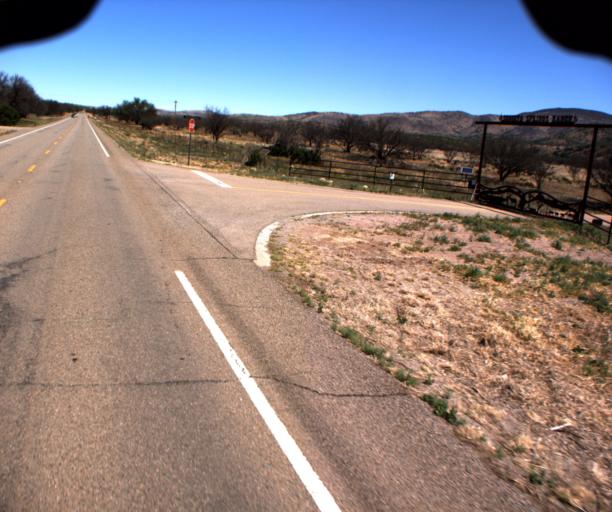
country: US
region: Arizona
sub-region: Santa Cruz County
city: Rio Rico
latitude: 31.5733
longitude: -110.7298
